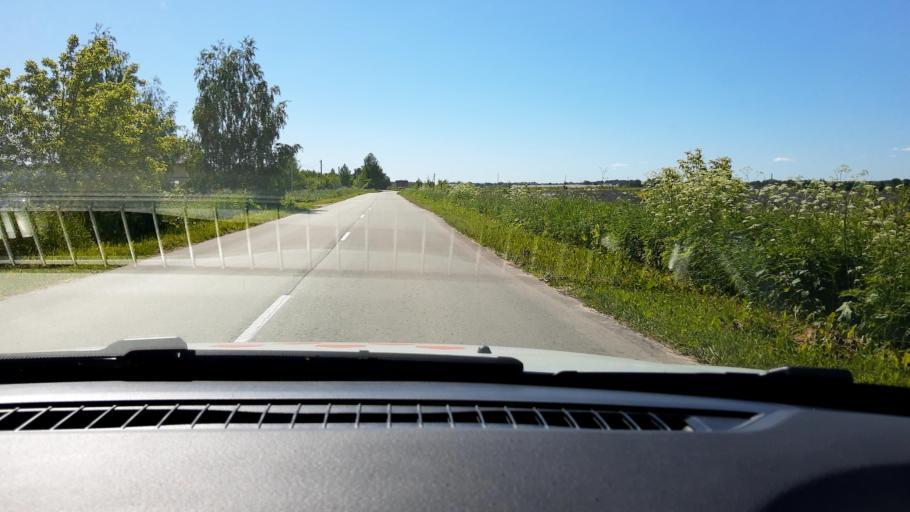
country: RU
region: Nizjnij Novgorod
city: Bor
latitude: 56.3955
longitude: 44.0608
